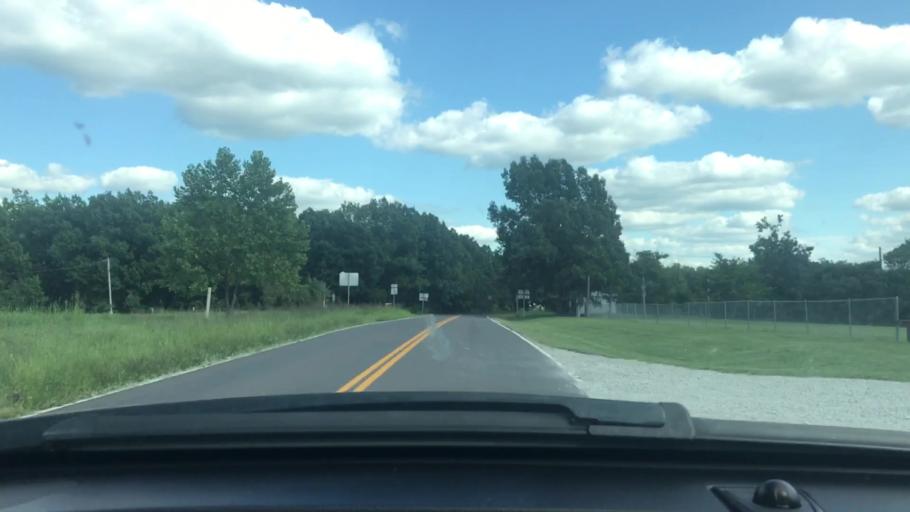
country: US
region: Missouri
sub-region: Wright County
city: Hartville
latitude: 37.3786
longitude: -92.3591
